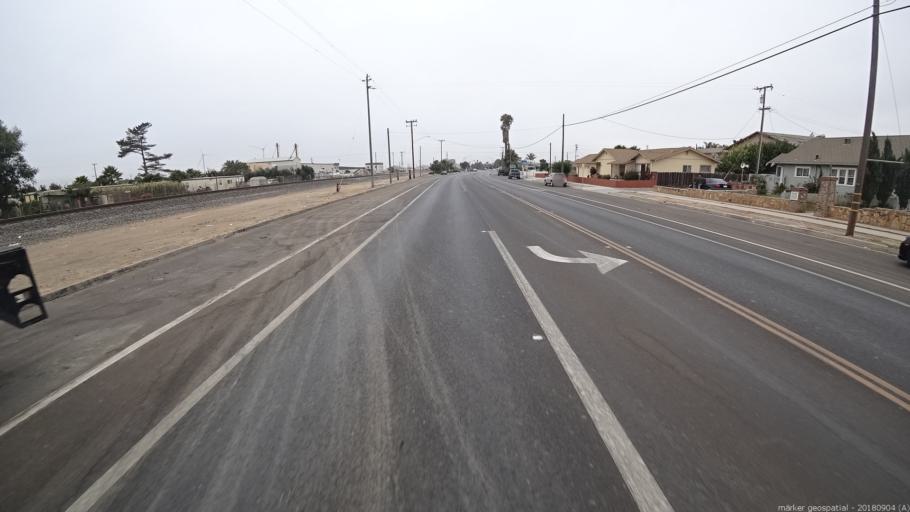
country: US
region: California
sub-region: Monterey County
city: Gonzales
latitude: 36.5022
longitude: -121.4401
